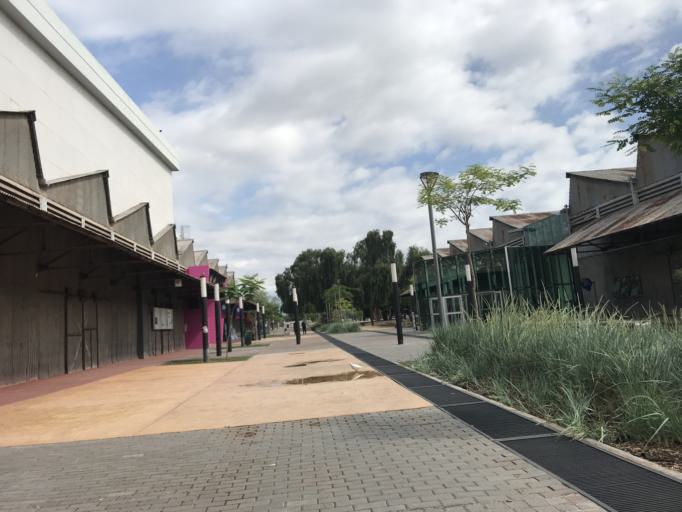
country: AR
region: Mendoza
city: Mendoza
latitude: -32.8782
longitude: -68.8398
